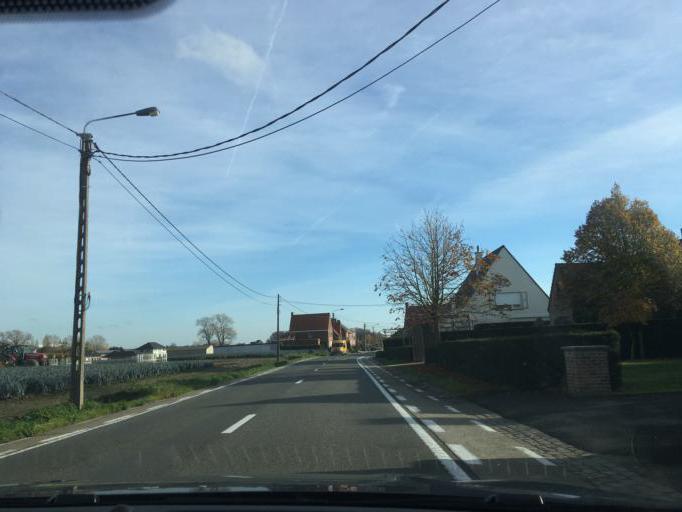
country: BE
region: Flanders
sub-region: Provincie West-Vlaanderen
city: Meulebeke
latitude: 50.9516
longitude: 3.2665
